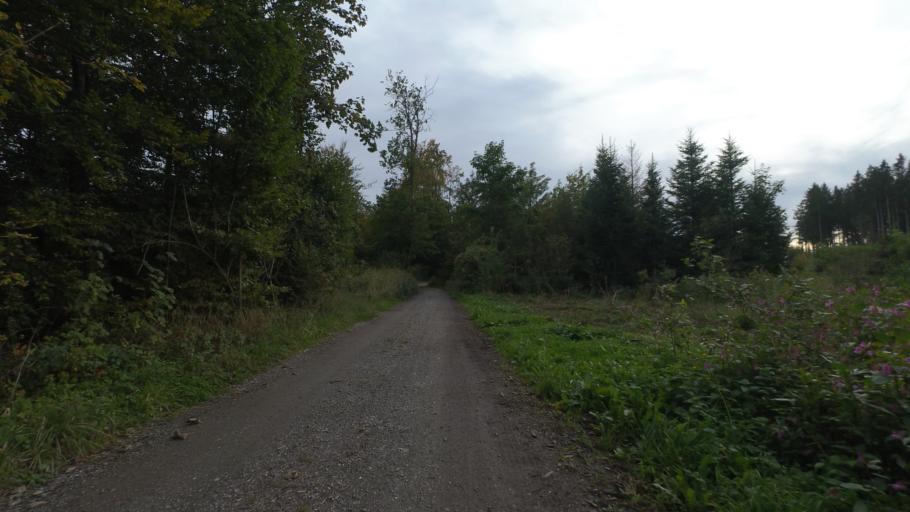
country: DE
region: Bavaria
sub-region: Upper Bavaria
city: Chieming
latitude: 47.9151
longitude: 12.5422
